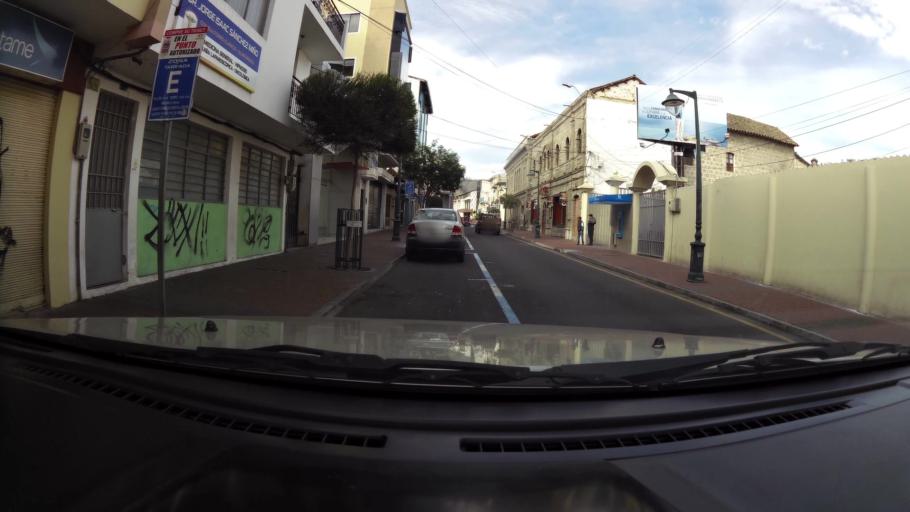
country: EC
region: Tungurahua
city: Ambato
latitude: -1.2448
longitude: -78.6272
